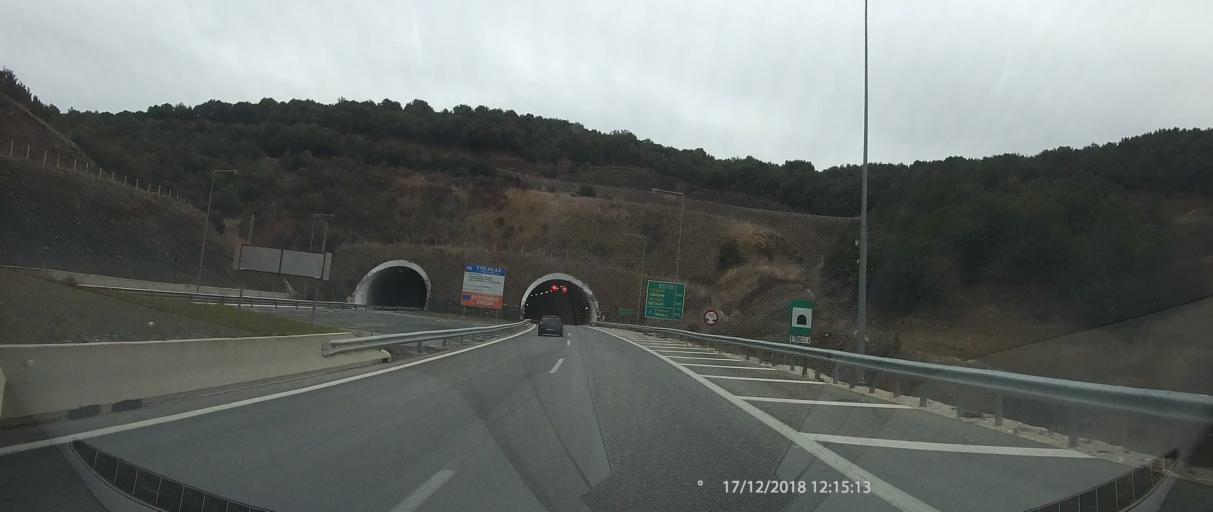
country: GR
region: Epirus
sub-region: Nomos Ioanninon
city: Katsikas
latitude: 39.7153
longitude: 21.0161
